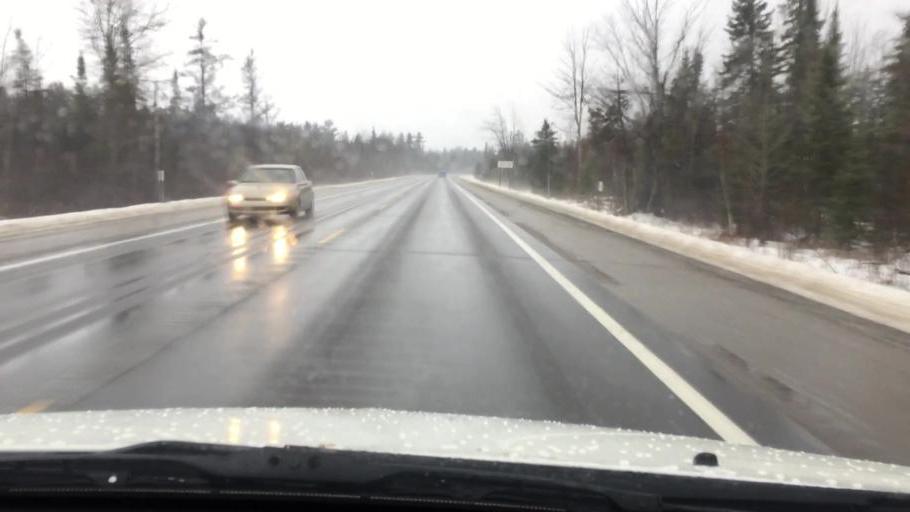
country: US
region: Michigan
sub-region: Kalkaska County
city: Kalkaska
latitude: 44.7055
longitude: -85.1993
